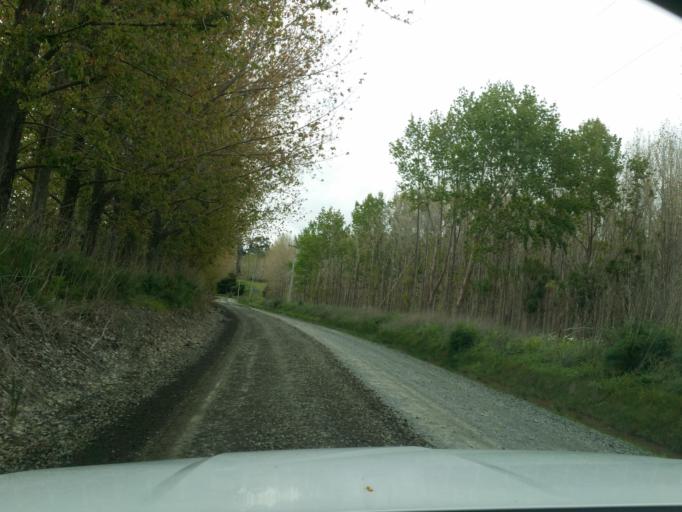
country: NZ
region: Northland
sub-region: Kaipara District
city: Dargaville
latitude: -35.9212
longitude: 173.9221
